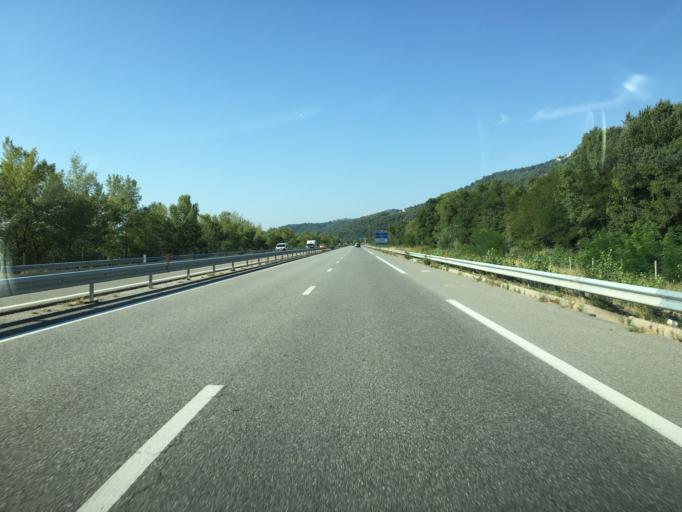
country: FR
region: Provence-Alpes-Cote d'Azur
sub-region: Departement des Alpes-de-Haute-Provence
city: Peyruis
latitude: 44.0074
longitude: 5.9310
